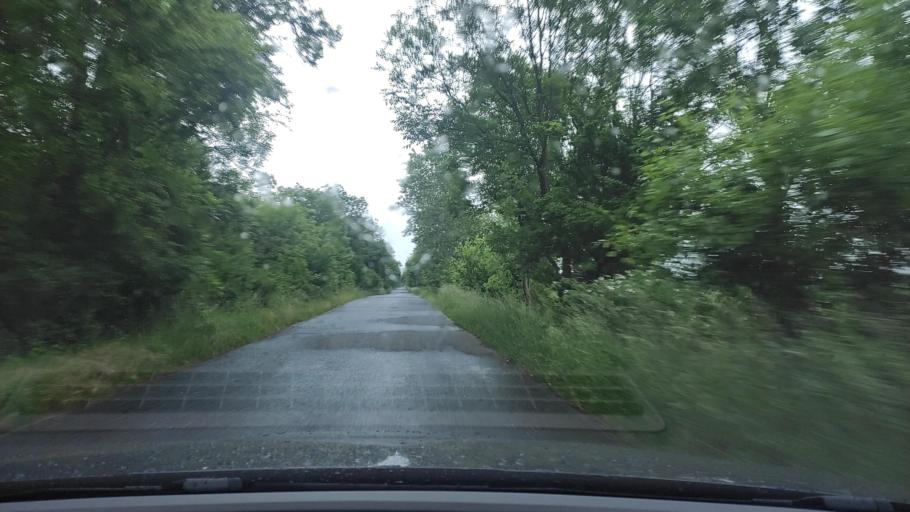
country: PL
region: Greater Poland Voivodeship
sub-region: Powiat poznanski
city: Kobylnica
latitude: 52.4969
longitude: 17.1151
